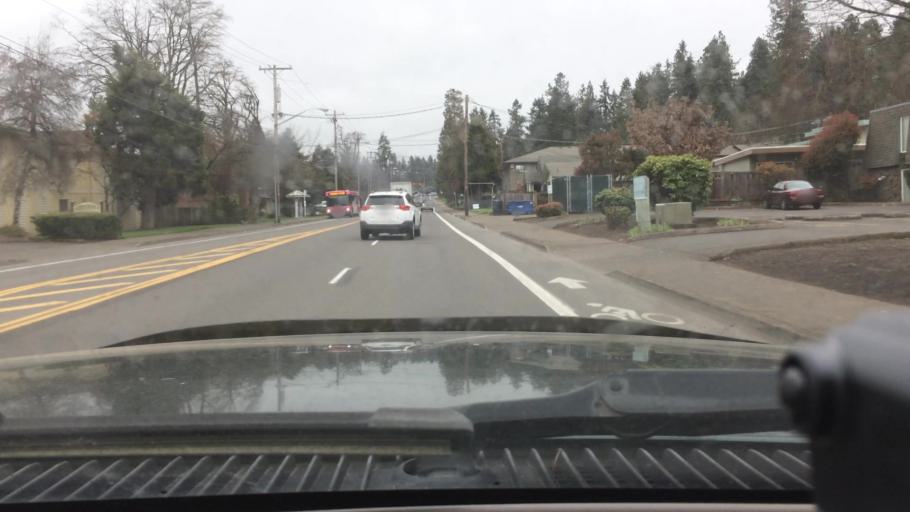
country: US
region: Oregon
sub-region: Lane County
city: Eugene
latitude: 44.0256
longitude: -123.0908
